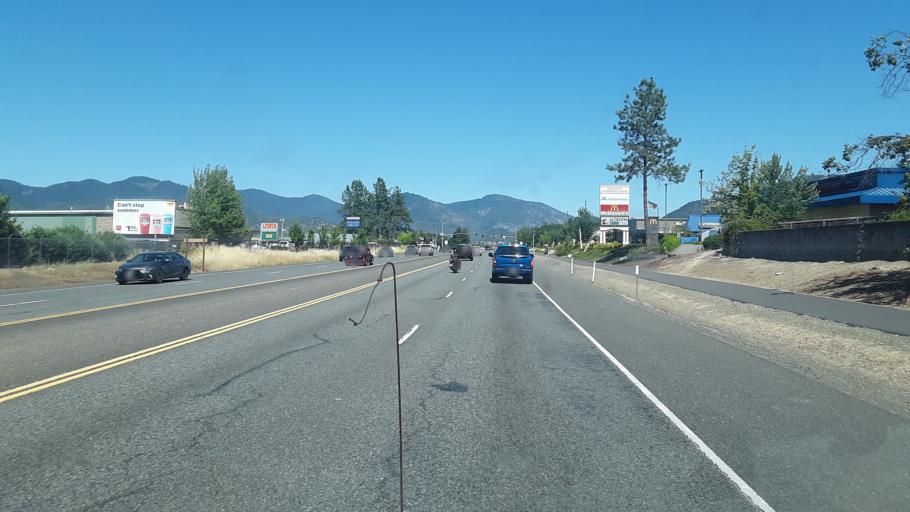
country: US
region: Oregon
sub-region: Josephine County
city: Grants Pass
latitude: 42.4206
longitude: -123.3555
